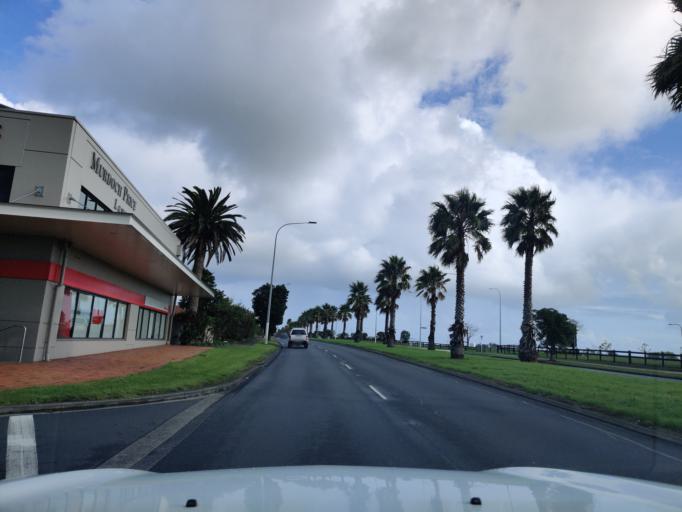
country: NZ
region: Auckland
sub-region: Auckland
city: Manukau City
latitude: -36.9652
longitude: 174.9017
